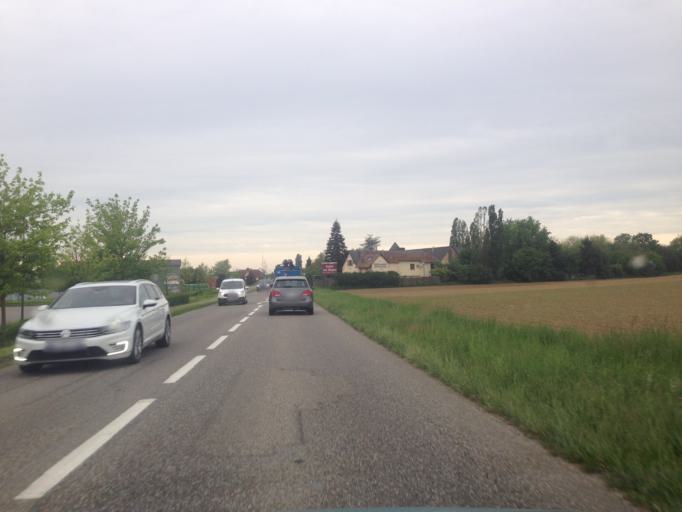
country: FR
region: Alsace
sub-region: Departement du Bas-Rhin
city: Mommenheim
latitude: 48.7532
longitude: 7.6606
